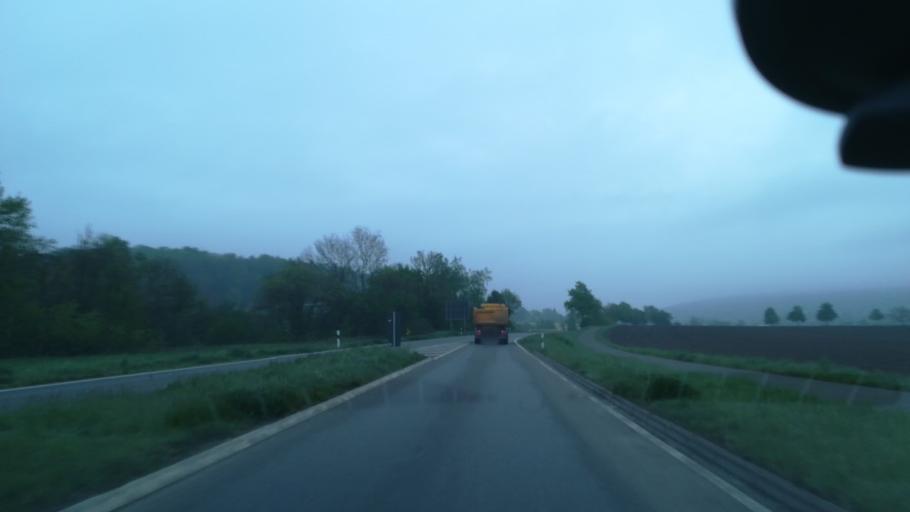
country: DE
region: Baden-Wuerttemberg
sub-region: Freiburg Region
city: Steisslingen
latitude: 47.7840
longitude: 8.9159
